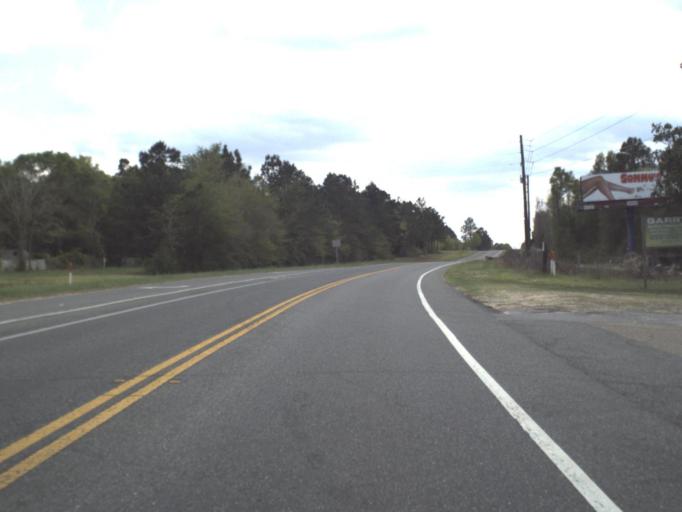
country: US
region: Florida
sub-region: Okaloosa County
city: Crestview
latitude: 30.8415
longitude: -86.5297
